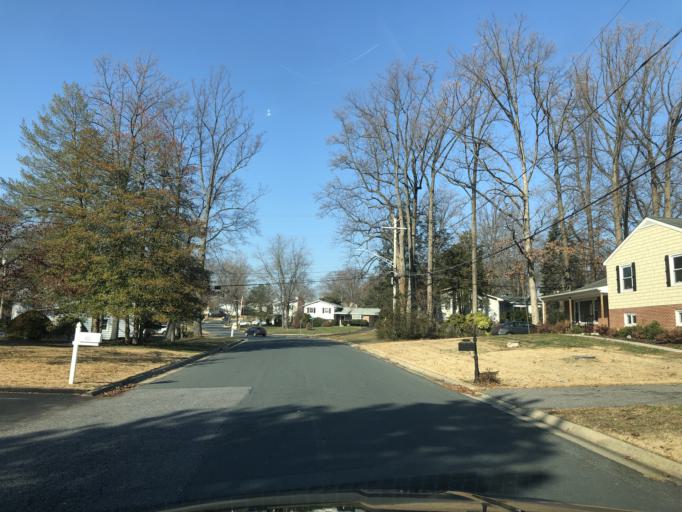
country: US
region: Maryland
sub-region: Anne Arundel County
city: Odenton
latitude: 39.0716
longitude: -76.6911
